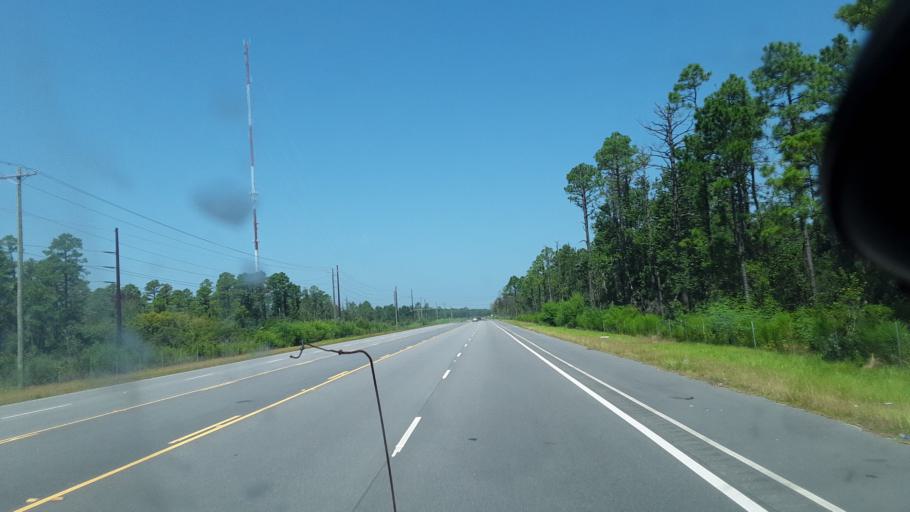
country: US
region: South Carolina
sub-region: Horry County
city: Myrtle Beach
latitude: 33.7814
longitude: -78.8750
